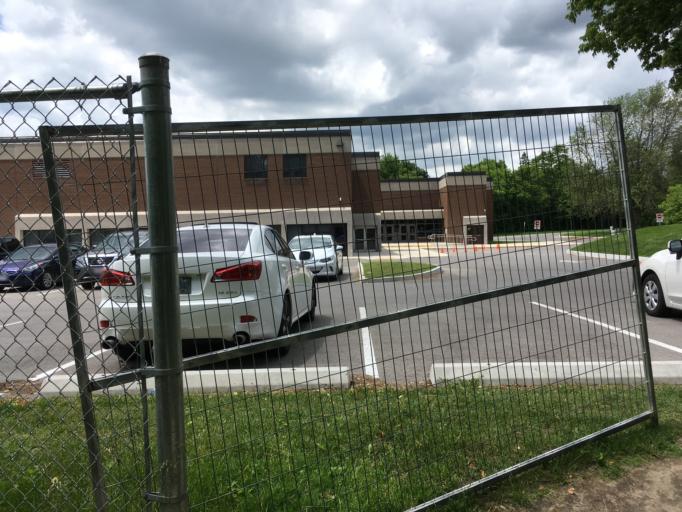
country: CA
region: Ontario
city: Oshawa
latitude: 43.8889
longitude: -78.8650
